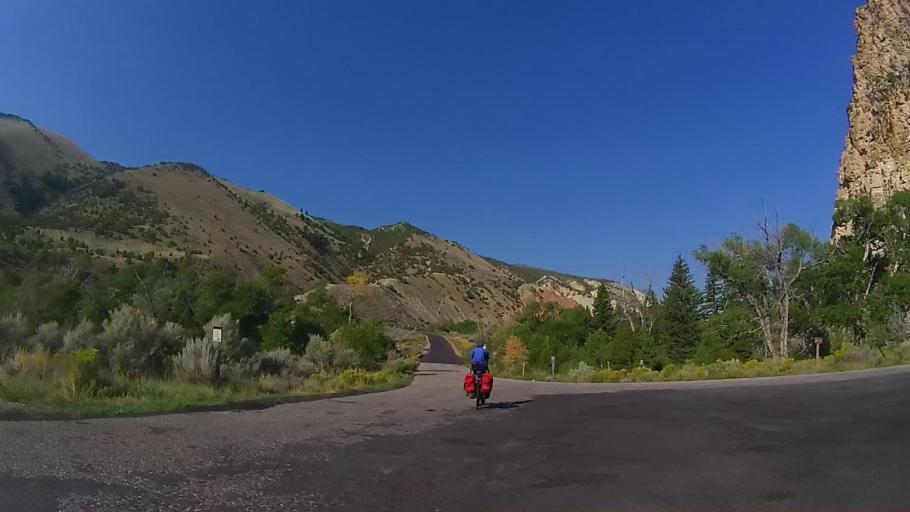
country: US
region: Utah
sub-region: Daggett County
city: Manila
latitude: 40.9310
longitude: -109.7249
